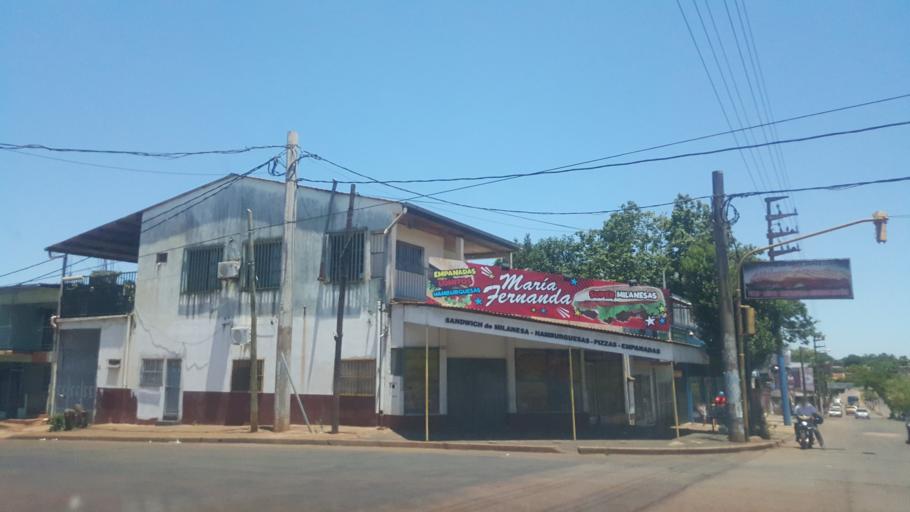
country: AR
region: Misiones
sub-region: Departamento de Capital
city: Posadas
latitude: -27.3998
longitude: -55.9134
